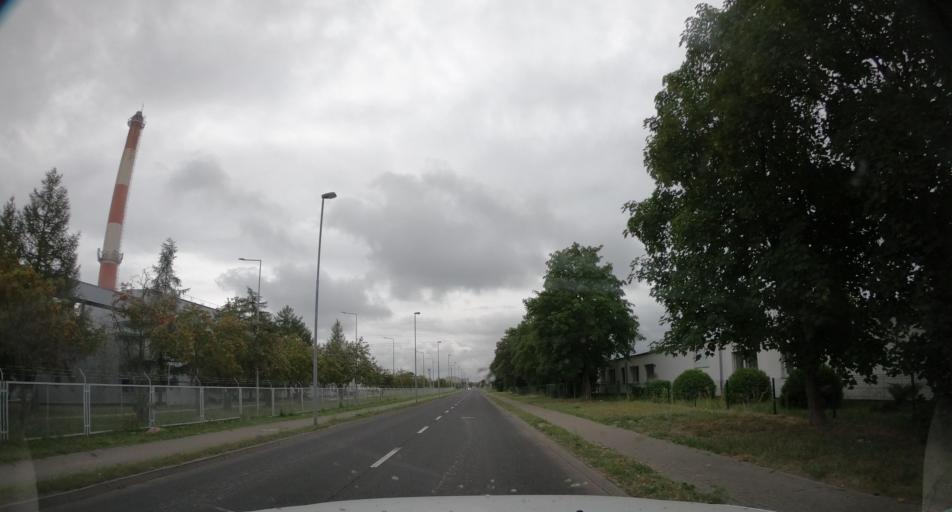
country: PL
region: West Pomeranian Voivodeship
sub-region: Powiat stargardzki
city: Stargard Szczecinski
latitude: 53.3504
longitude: 15.0032
